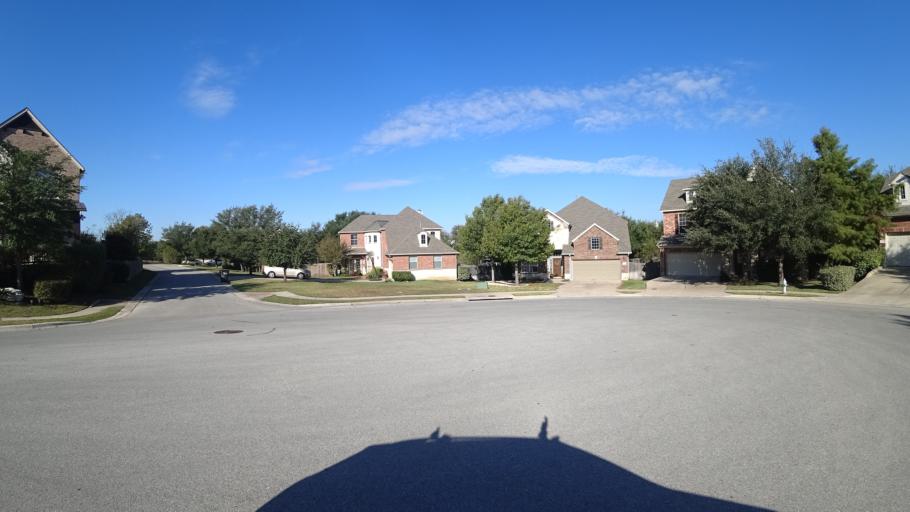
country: US
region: Texas
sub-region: Travis County
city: Hudson Bend
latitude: 30.3678
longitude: -97.8982
